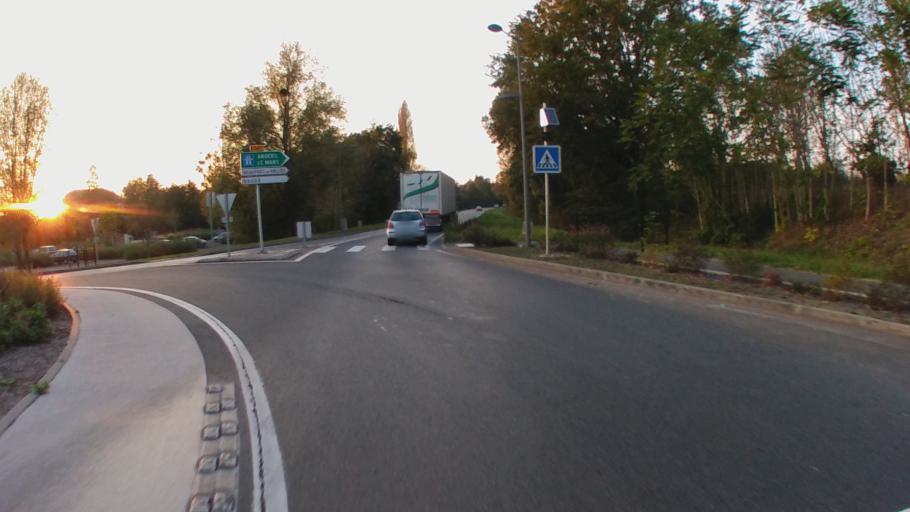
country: FR
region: Pays de la Loire
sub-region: Departement de Maine-et-Loire
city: Jumelles
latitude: 47.3822
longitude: -0.1076
